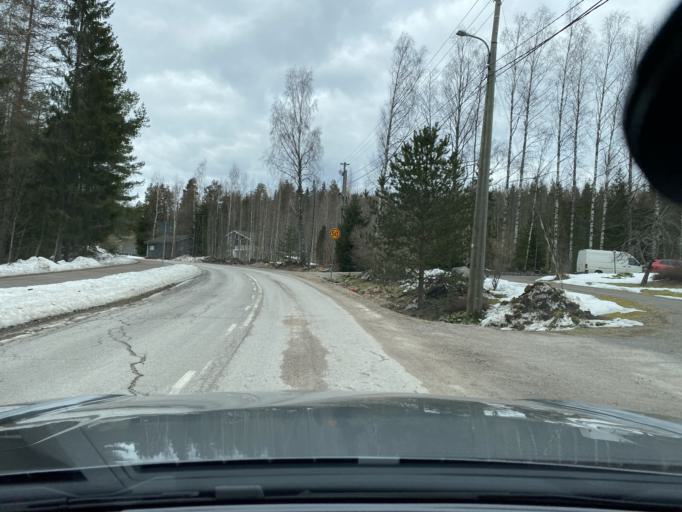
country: FI
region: Uusimaa
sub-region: Helsinki
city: Hyvinge
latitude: 60.5704
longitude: 24.7982
